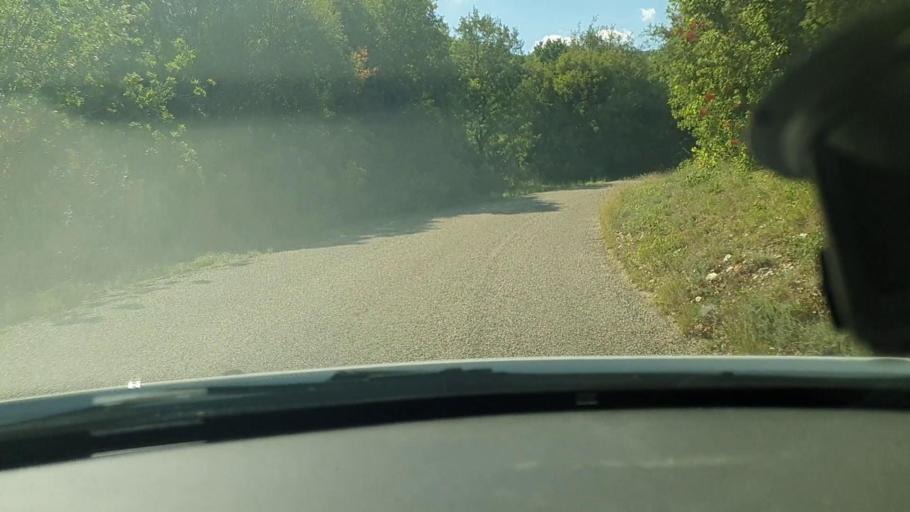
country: FR
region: Languedoc-Roussillon
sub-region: Departement du Gard
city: Goudargues
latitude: 44.1587
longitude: 4.4296
